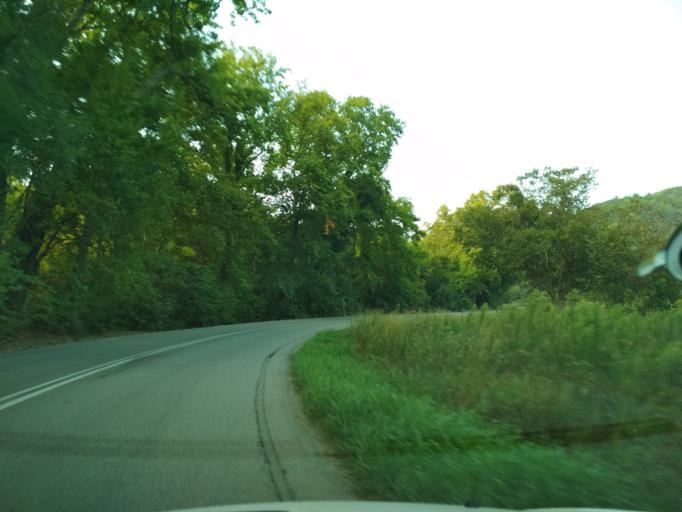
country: GR
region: Central Greece
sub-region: Nomos Evvoias
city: Prokopion
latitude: 38.7663
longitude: 23.4782
